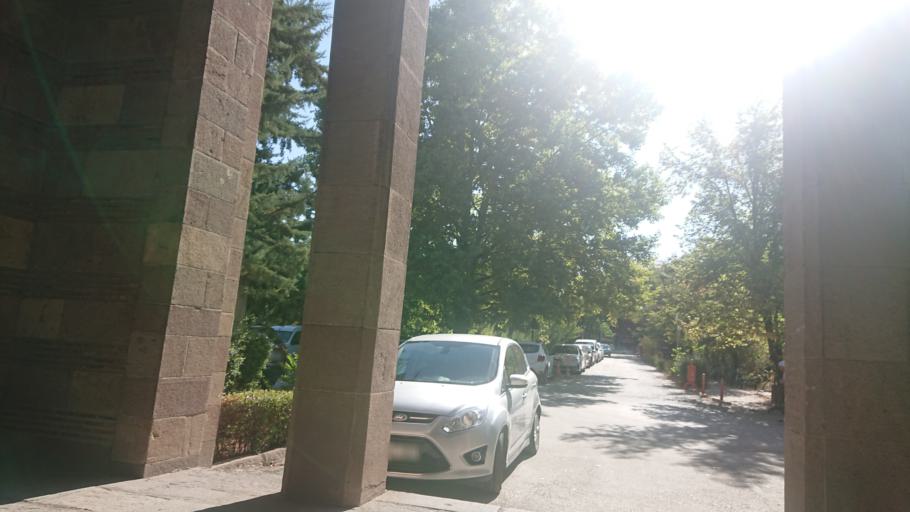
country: TR
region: Ankara
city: Ankara
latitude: 39.9346
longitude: 32.8318
